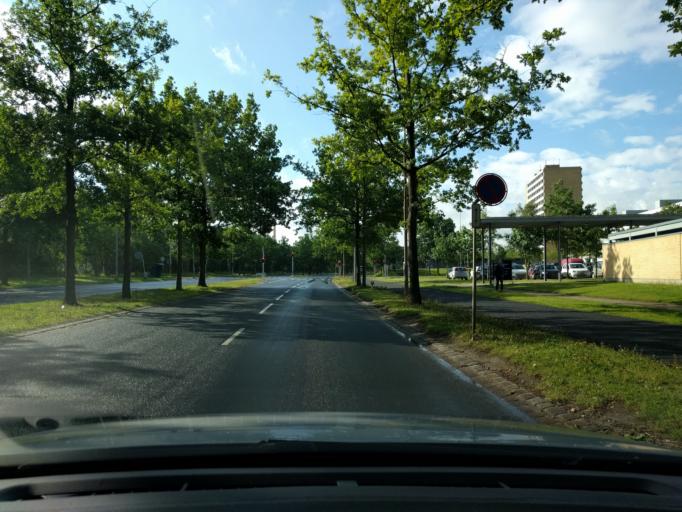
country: DK
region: South Denmark
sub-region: Odense Kommune
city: Seden
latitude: 55.4104
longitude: 10.4420
